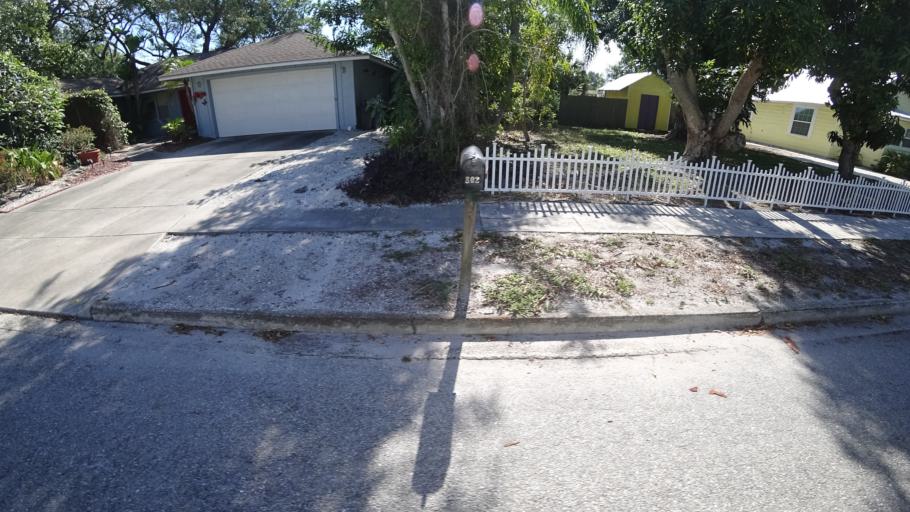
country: US
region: Florida
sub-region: Manatee County
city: West Bradenton
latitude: 27.5064
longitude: -82.6455
